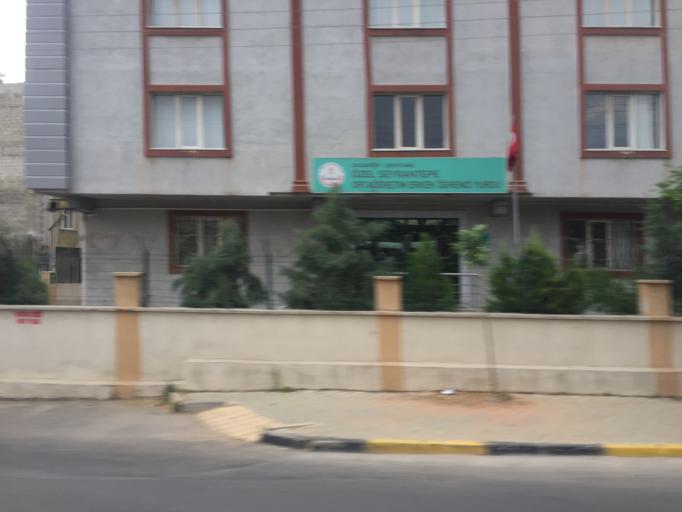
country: TR
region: Gaziantep
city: Gaziantep
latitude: 37.0635
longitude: 37.4152
